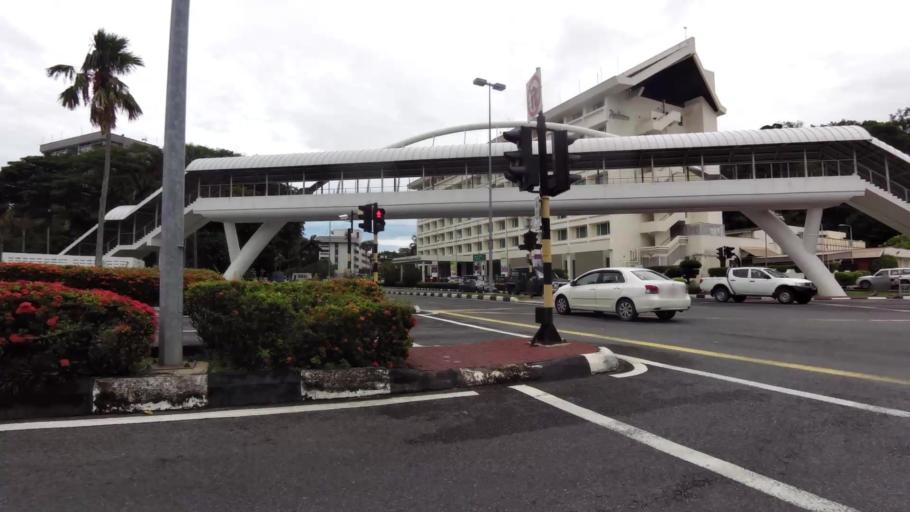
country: BN
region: Brunei and Muara
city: Bandar Seri Begawan
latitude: 4.8938
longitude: 114.9426
